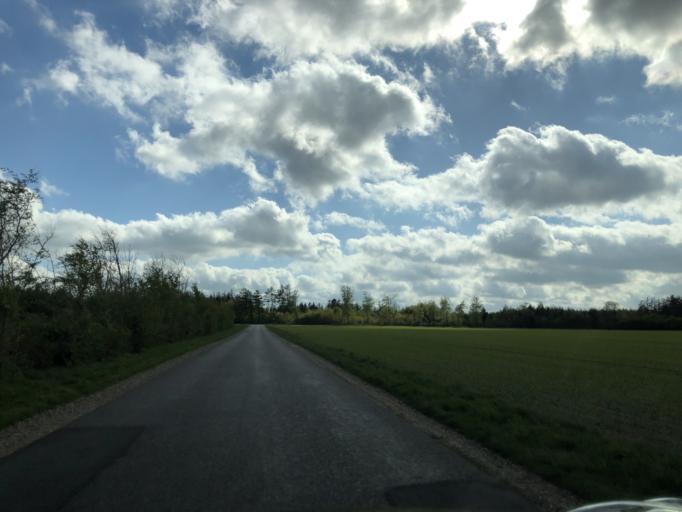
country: DK
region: Central Jutland
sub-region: Holstebro Kommune
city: Holstebro
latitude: 56.3034
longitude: 8.6978
